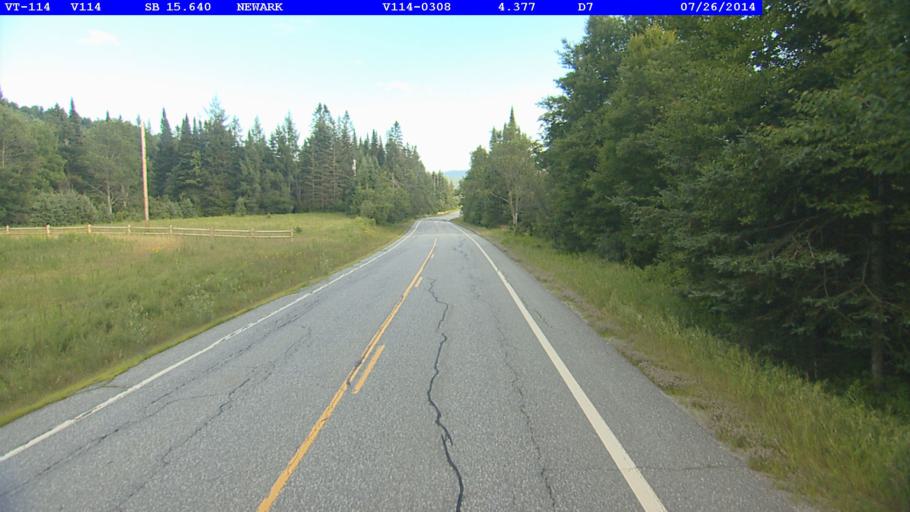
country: US
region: Vermont
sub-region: Caledonia County
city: Lyndonville
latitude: 44.7289
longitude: -71.8753
